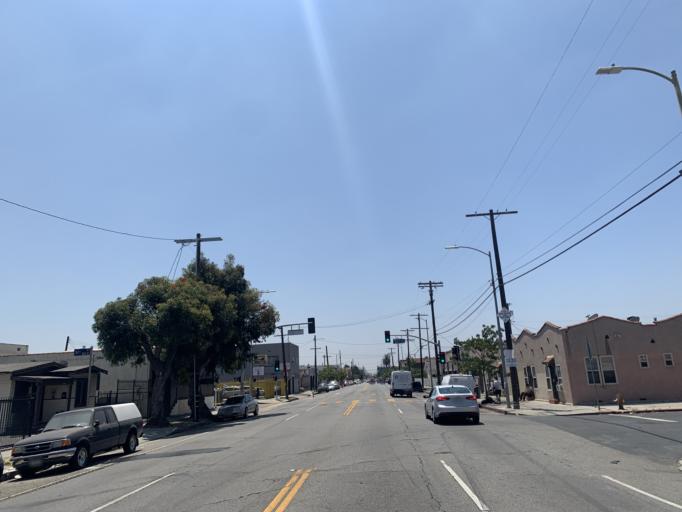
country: US
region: California
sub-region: Los Angeles County
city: Florence-Graham
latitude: 33.9956
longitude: -118.2871
